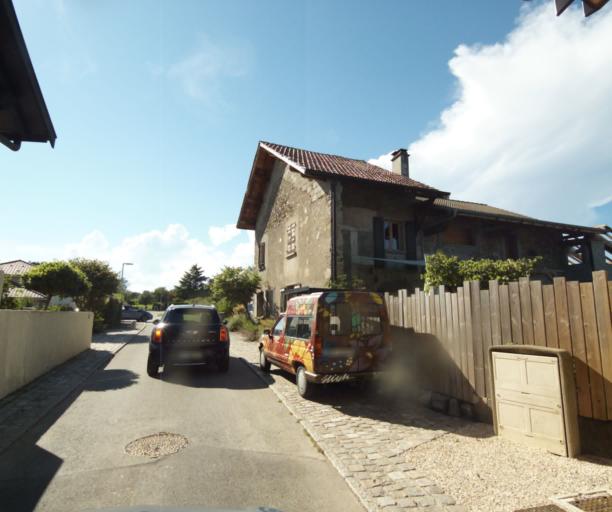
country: FR
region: Rhone-Alpes
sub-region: Departement de la Haute-Savoie
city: Messery
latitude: 46.3311
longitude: 6.3043
